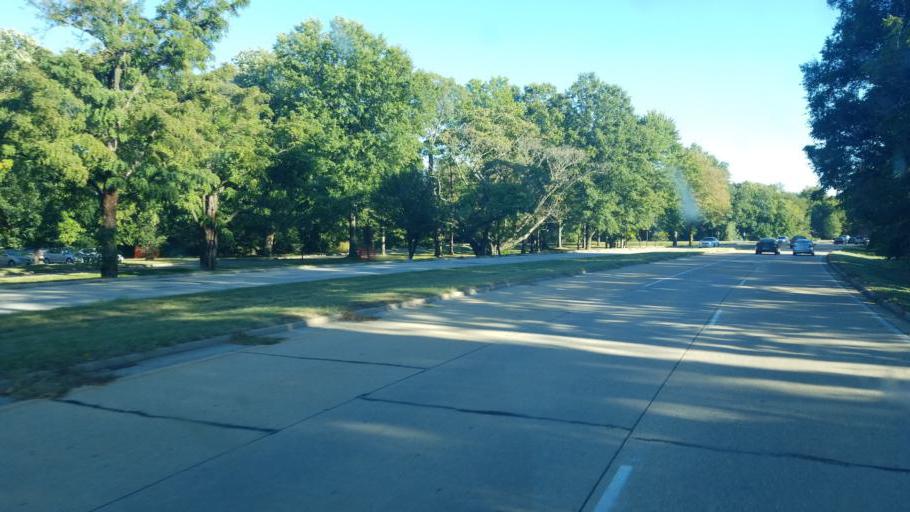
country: US
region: Virginia
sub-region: Fairfax County
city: Belle Haven
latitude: 38.7791
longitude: -77.0526
